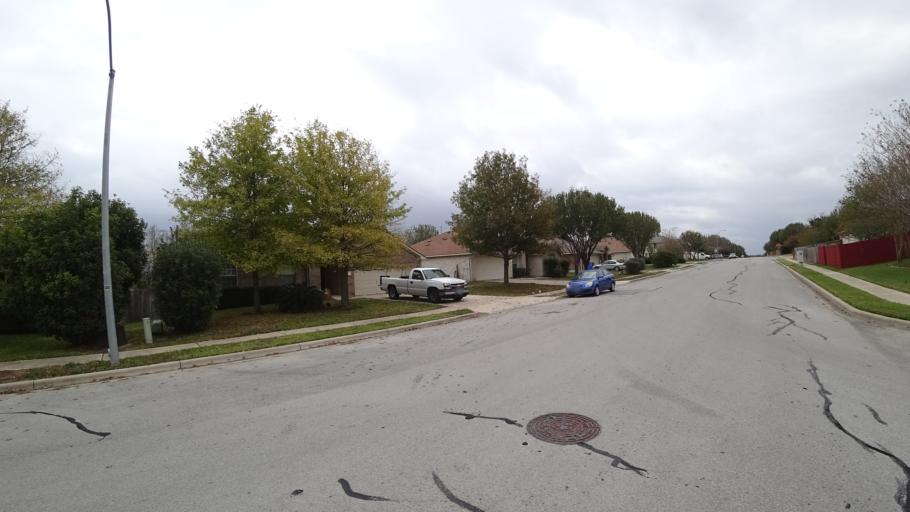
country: US
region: Texas
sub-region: Travis County
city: Pflugerville
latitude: 30.4387
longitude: -97.6027
